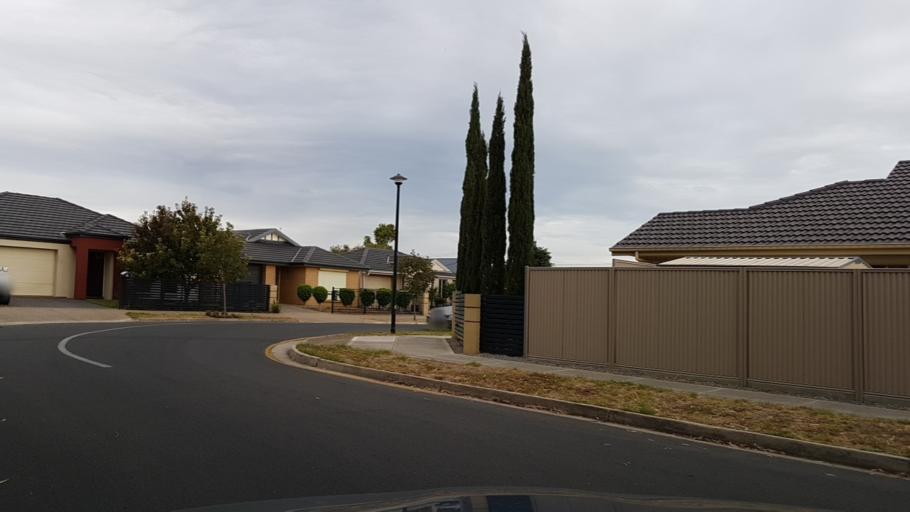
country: AU
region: South Australia
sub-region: Charles Sturt
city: Woodville North
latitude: -34.8610
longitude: 138.5412
